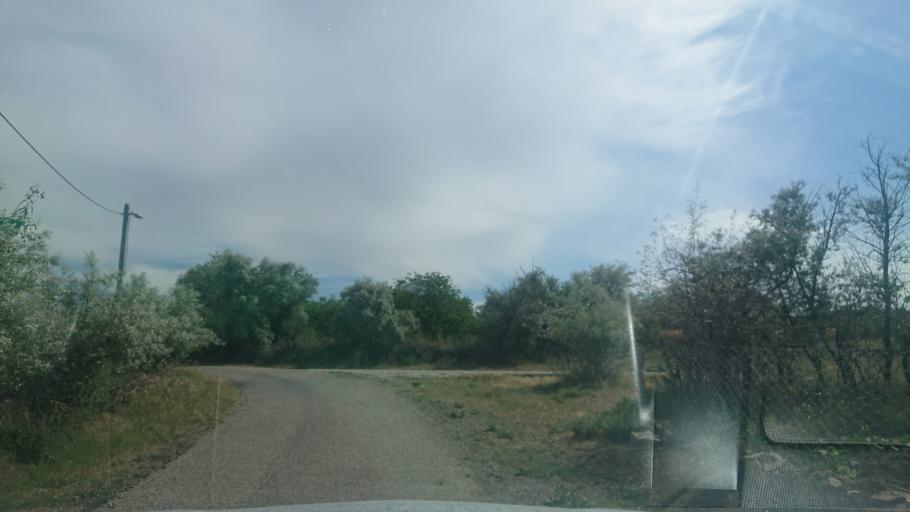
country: TR
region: Aksaray
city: Ortakoy
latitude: 38.8203
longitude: 34.0032
